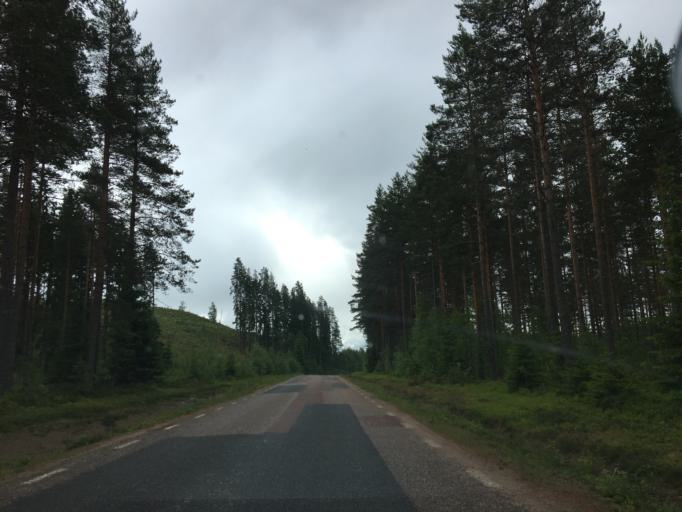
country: SE
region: OErebro
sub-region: Hallefors Kommun
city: Haellefors
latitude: 60.0682
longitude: 14.4934
